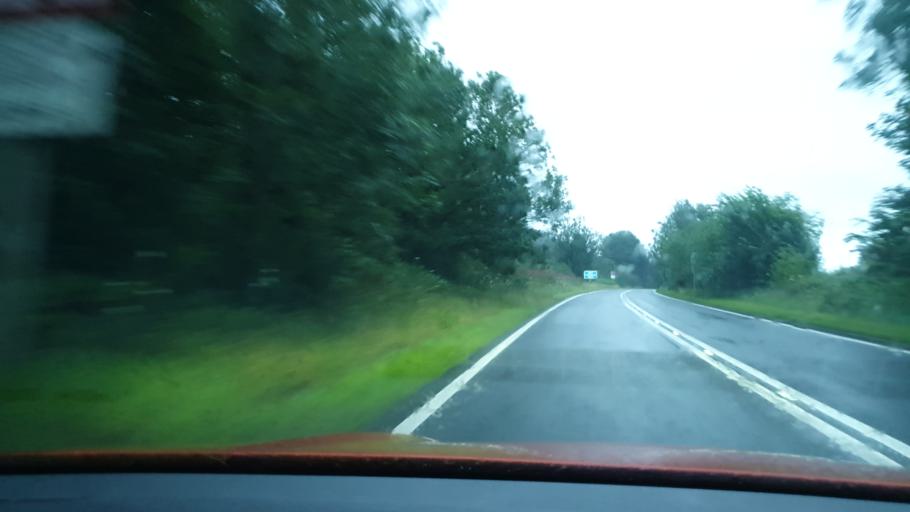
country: GB
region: England
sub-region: Cumbria
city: Grange-over-Sands
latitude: 54.2561
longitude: -2.9465
